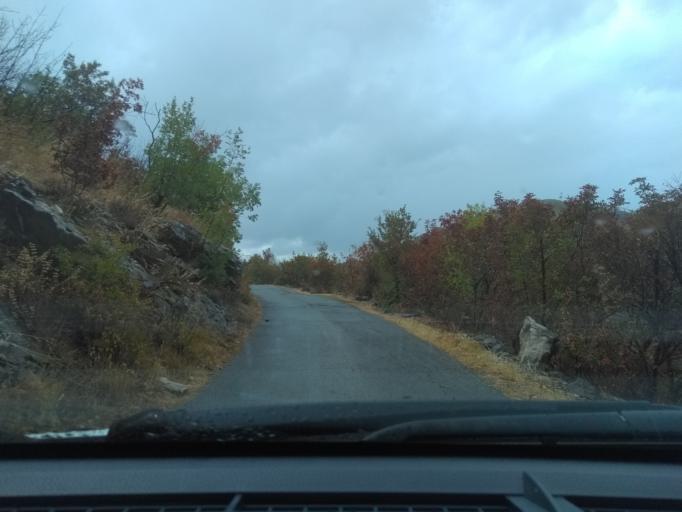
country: ME
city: Stari Bar
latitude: 42.1844
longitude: 19.1734
